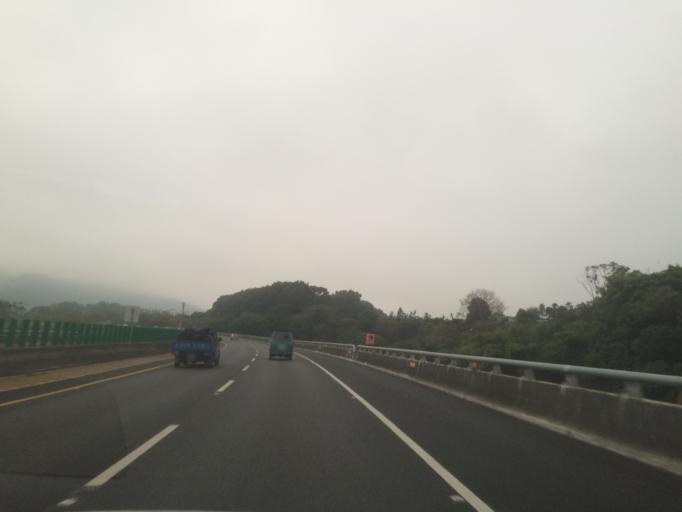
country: TW
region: Taiwan
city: Zhongxing New Village
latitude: 23.9886
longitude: 120.7832
